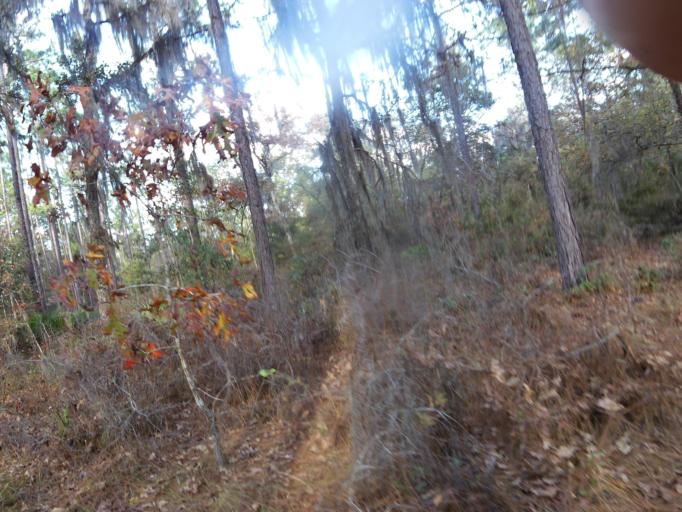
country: US
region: Florida
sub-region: Clay County
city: Middleburg
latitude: 30.1443
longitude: -81.9587
